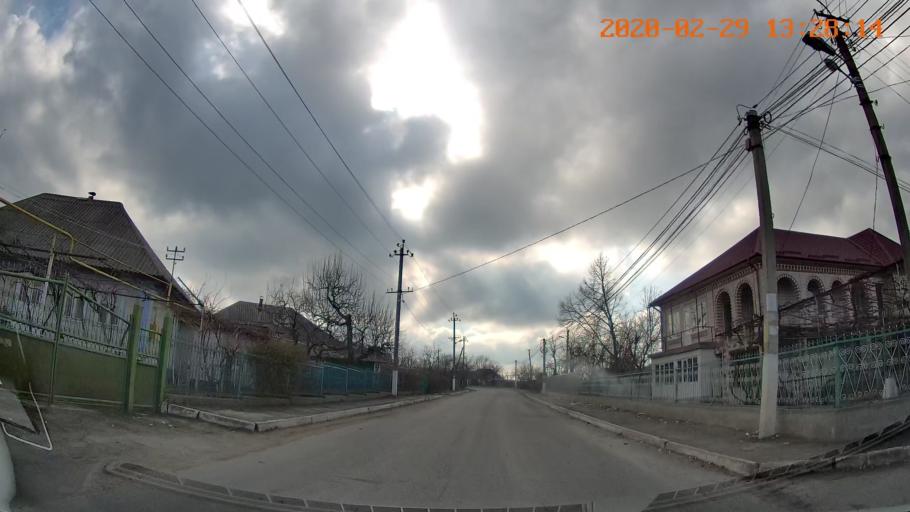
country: MD
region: Telenesti
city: Camenca
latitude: 47.9070
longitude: 28.6433
